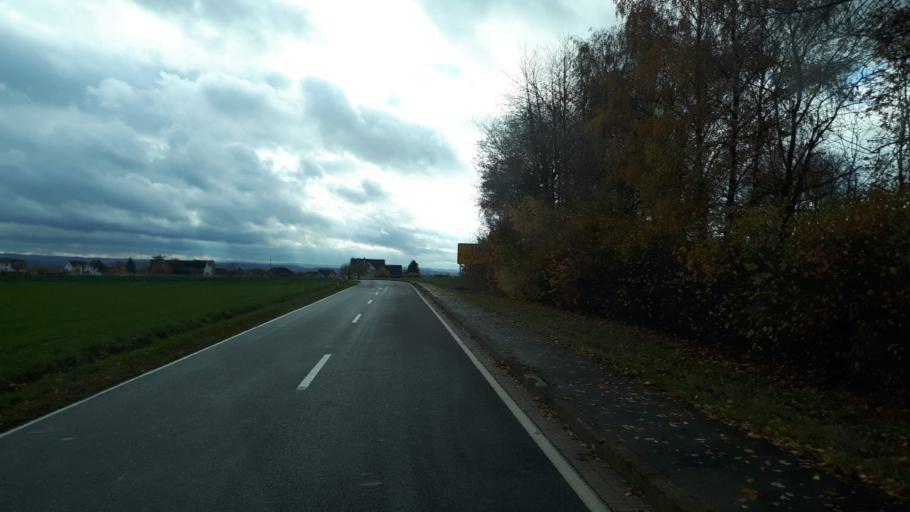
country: DE
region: Rheinland-Pfalz
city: Binningen
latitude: 50.2132
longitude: 7.2497
